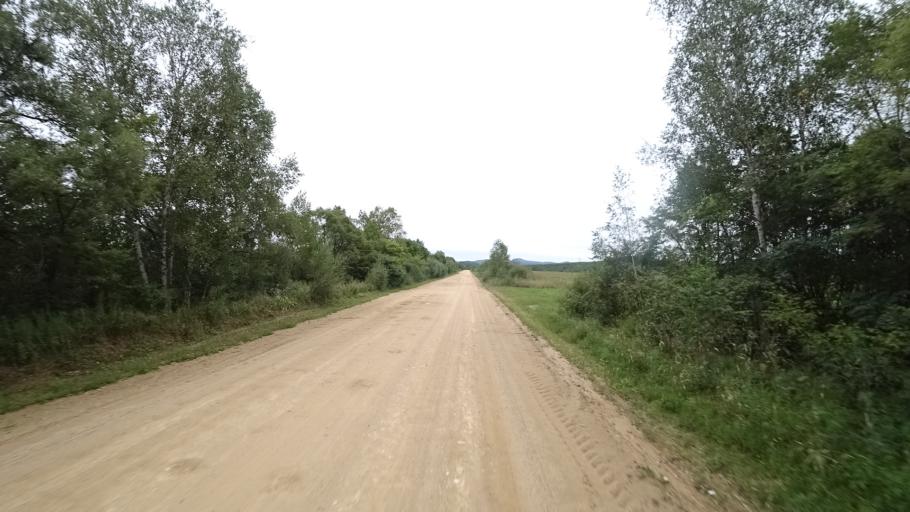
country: RU
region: Primorskiy
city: Rettikhovka
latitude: 44.1595
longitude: 132.7004
